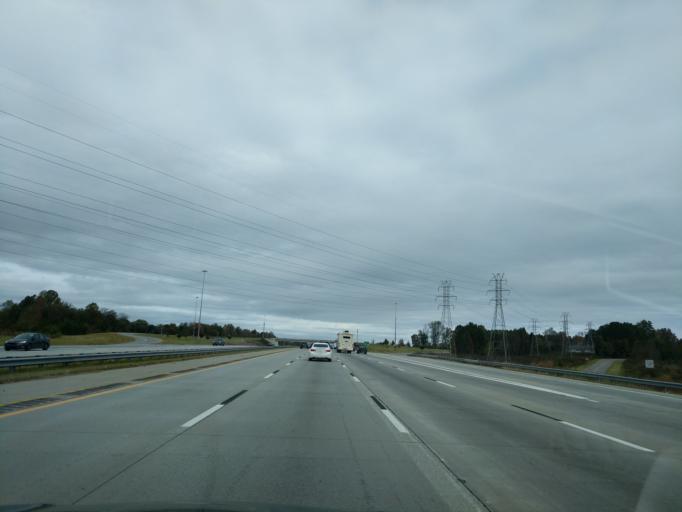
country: US
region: North Carolina
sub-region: Rowan County
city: East Spencer
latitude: 35.6901
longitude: -80.4029
